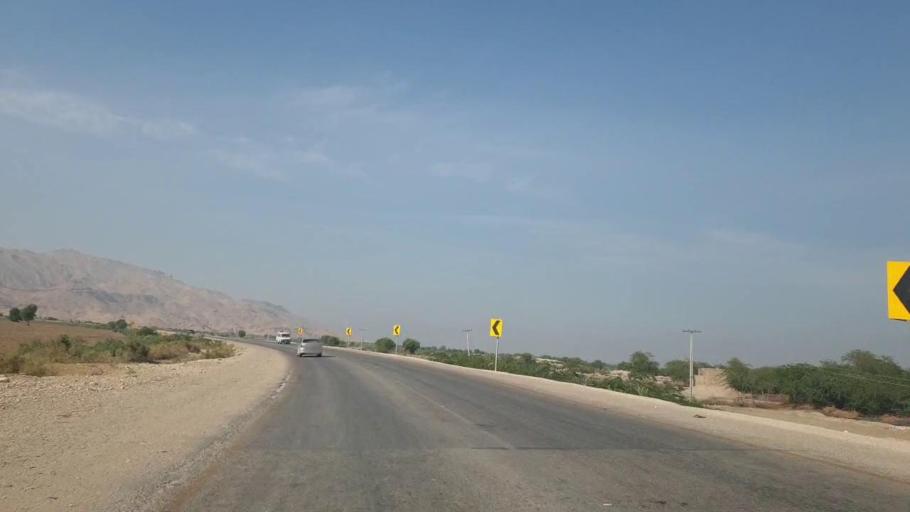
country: PK
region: Sindh
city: Sehwan
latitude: 26.2685
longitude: 67.9037
